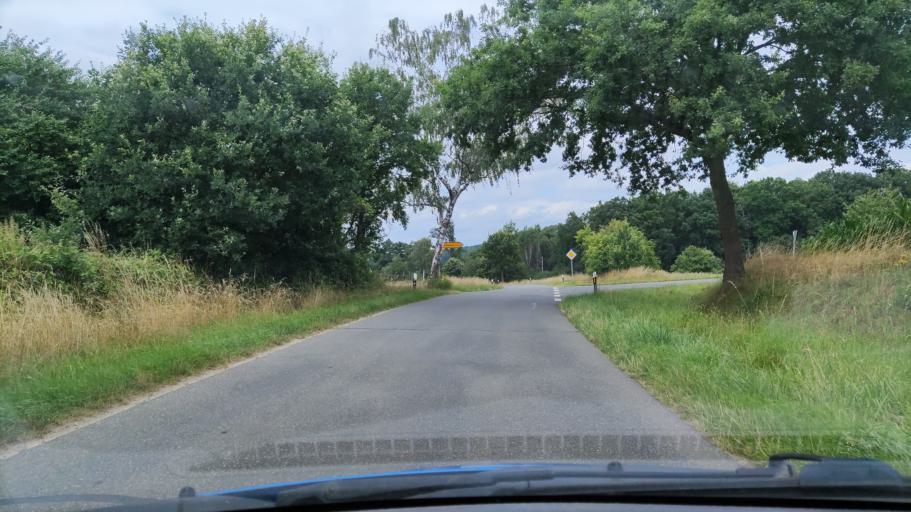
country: DE
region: Lower Saxony
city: Weste
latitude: 53.0691
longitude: 10.6926
